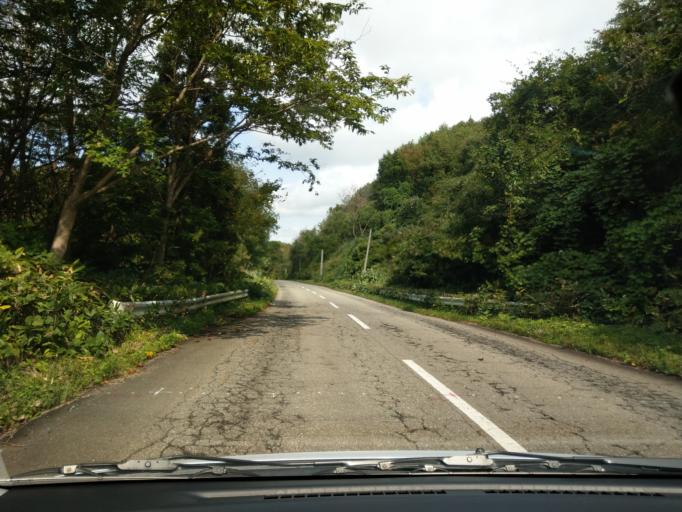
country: JP
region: Akita
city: Omagari
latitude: 39.4888
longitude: 140.3138
